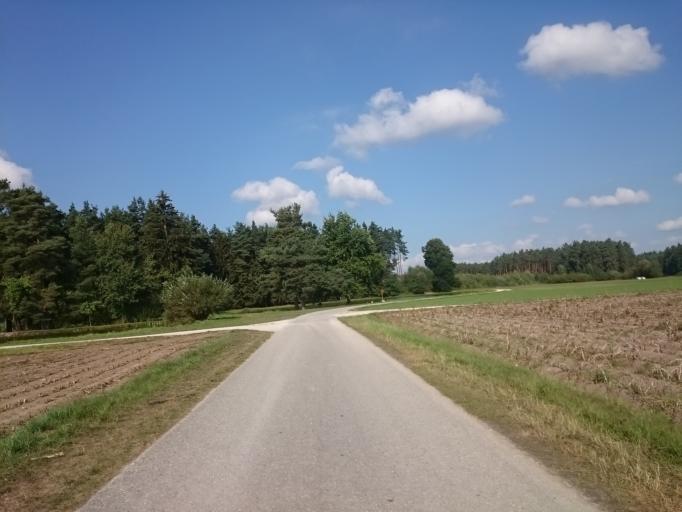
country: DE
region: Bavaria
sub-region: Regierungsbezirk Mittelfranken
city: Hilpoltstein
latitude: 49.1584
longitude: 11.1693
